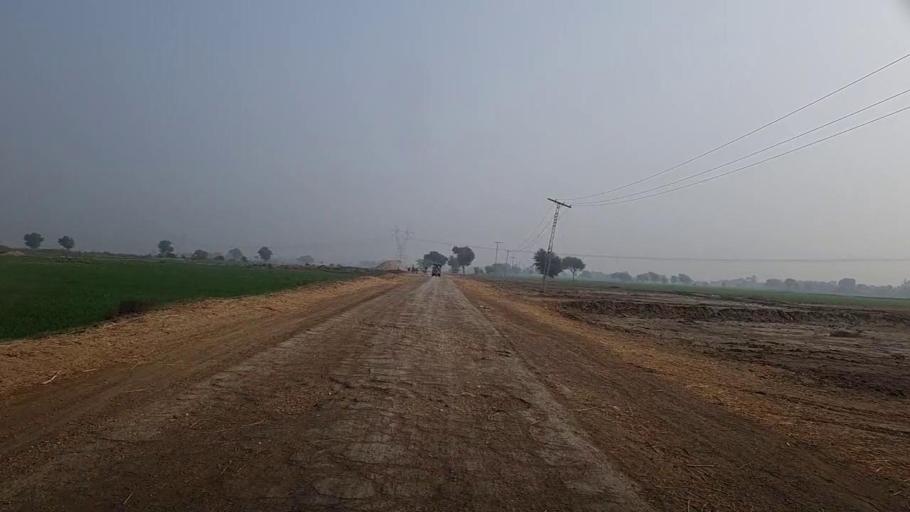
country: PK
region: Sindh
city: Phulji
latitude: 26.8261
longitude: 67.7568
